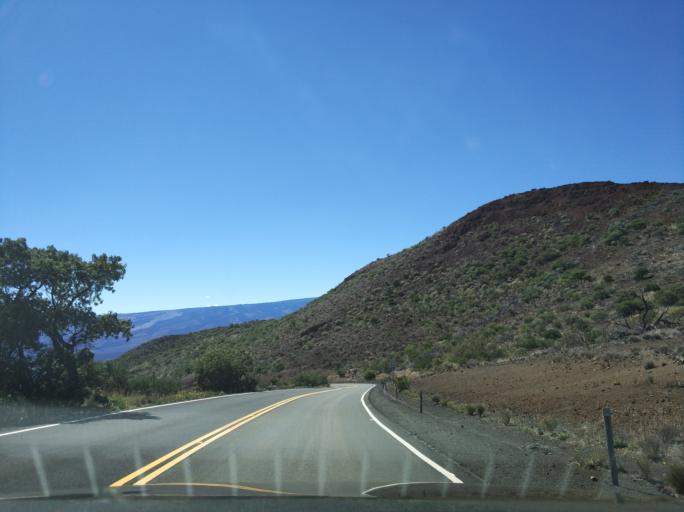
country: US
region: Hawaii
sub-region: Hawaii County
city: Honoka'a
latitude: 19.7564
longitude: -155.4565
